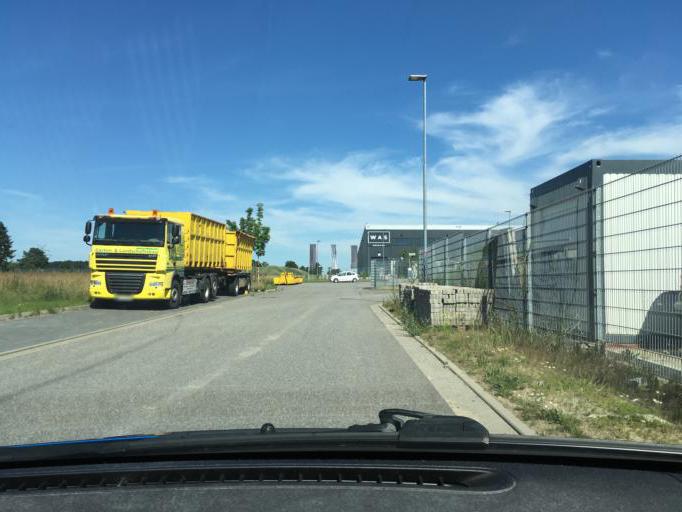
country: DE
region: Lower Saxony
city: Buchholz in der Nordheide
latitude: 53.3748
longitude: 9.9059
